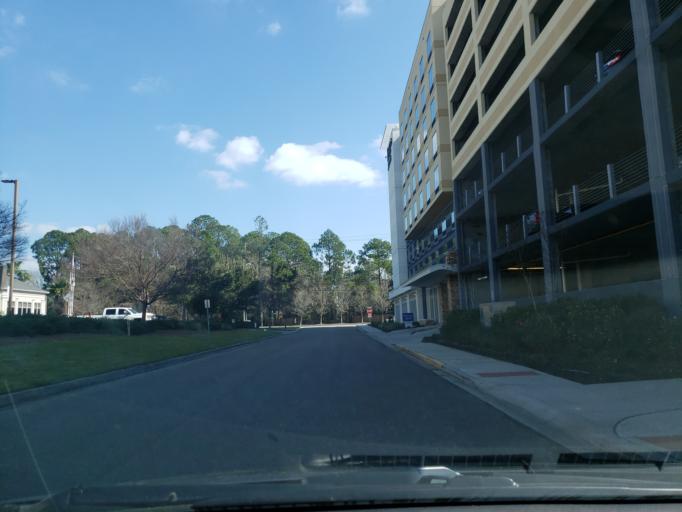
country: US
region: Georgia
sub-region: Chatham County
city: Savannah
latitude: 32.0225
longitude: -81.1115
